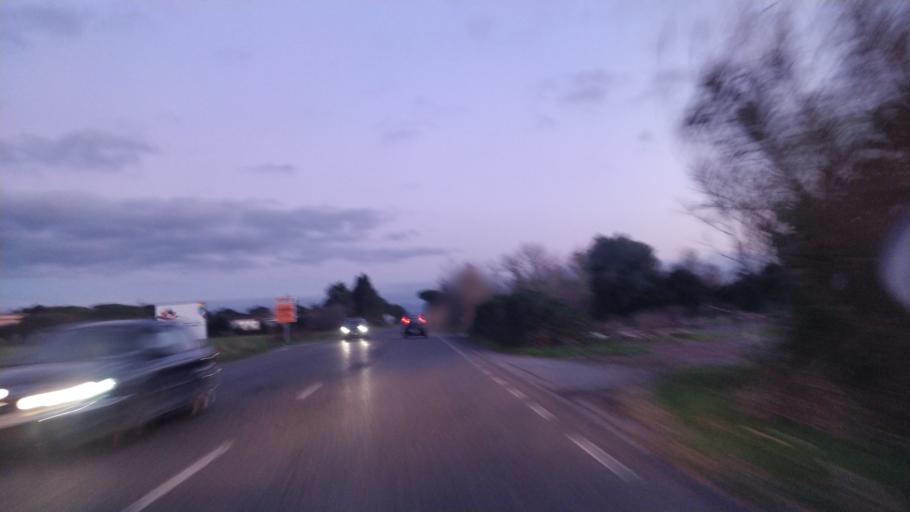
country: IT
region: Tuscany
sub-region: Provincia di Livorno
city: Vada
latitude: 43.3439
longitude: 10.4730
